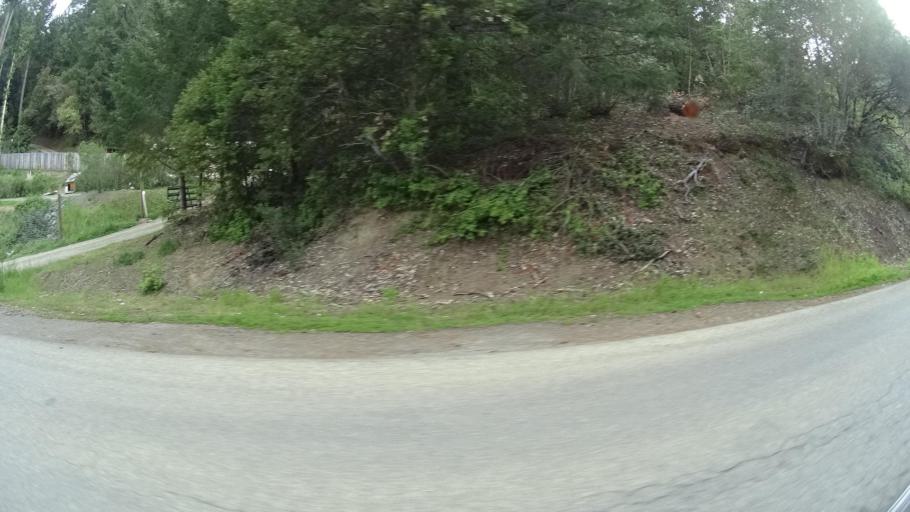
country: US
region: California
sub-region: Humboldt County
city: Redway
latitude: 40.2956
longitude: -123.8262
